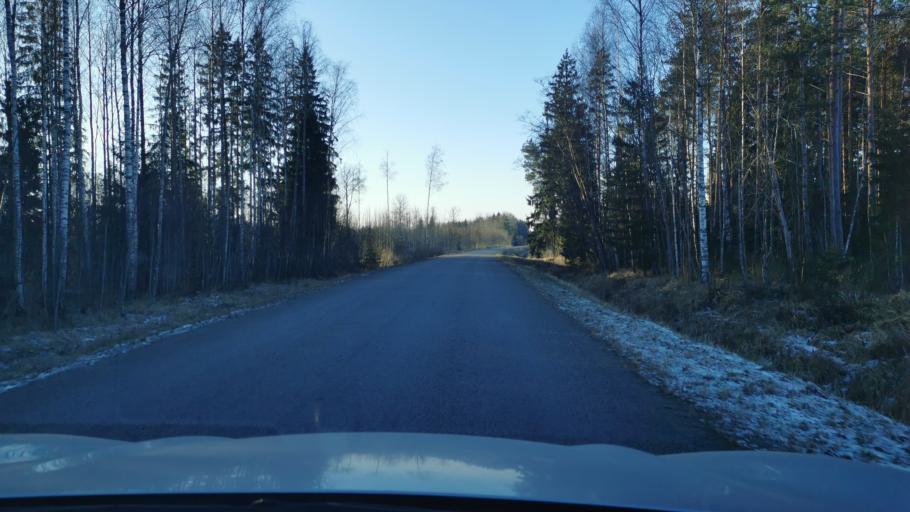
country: EE
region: Ida-Virumaa
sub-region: Kivioli linn
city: Kivioli
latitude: 59.2158
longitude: 26.9434
